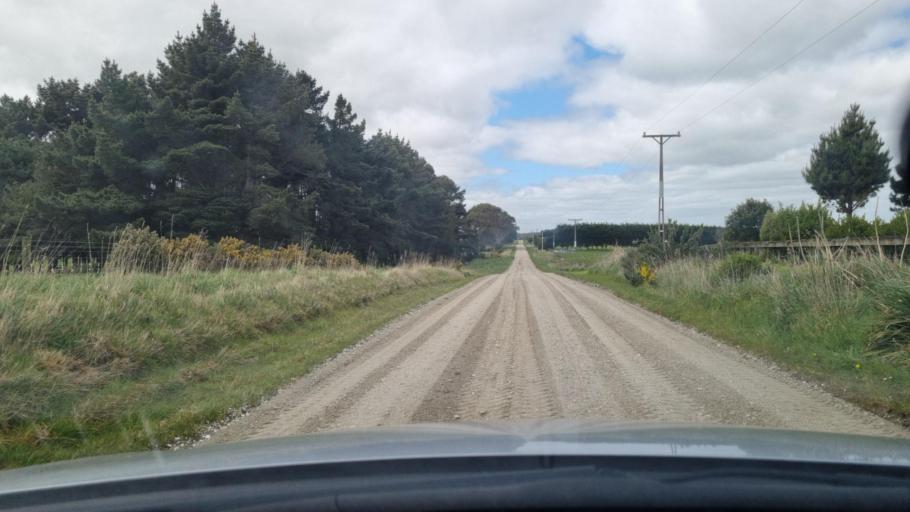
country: NZ
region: Southland
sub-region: Invercargill City
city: Invercargill
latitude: -46.4342
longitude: 168.4040
